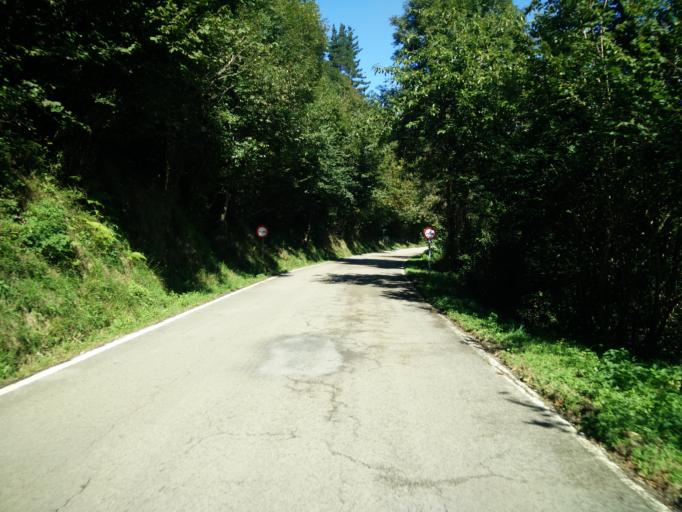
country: ES
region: Cantabria
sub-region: Provincia de Cantabria
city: Ruente
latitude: 43.1409
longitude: -4.2898
